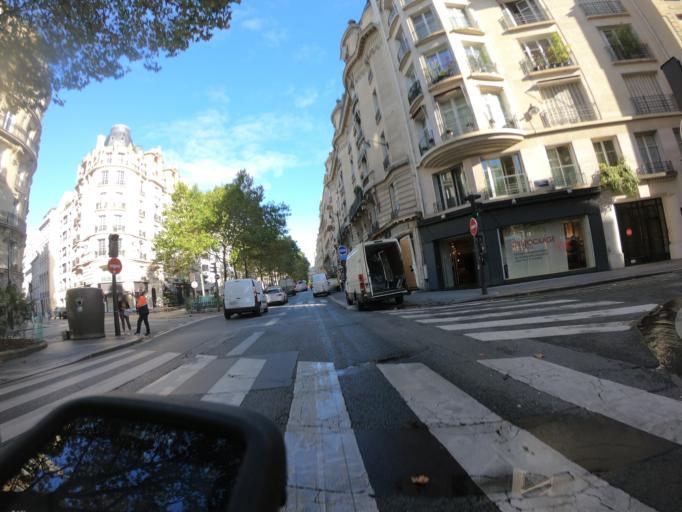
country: FR
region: Ile-de-France
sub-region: Paris
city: Paris
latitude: 48.8531
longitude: 2.3265
